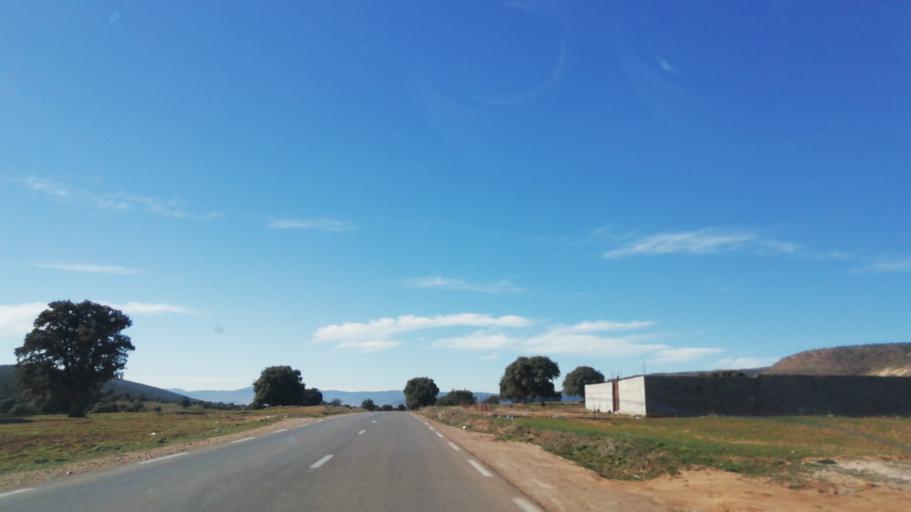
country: DZ
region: Tlemcen
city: Sebdou
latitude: 34.6997
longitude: -1.2289
